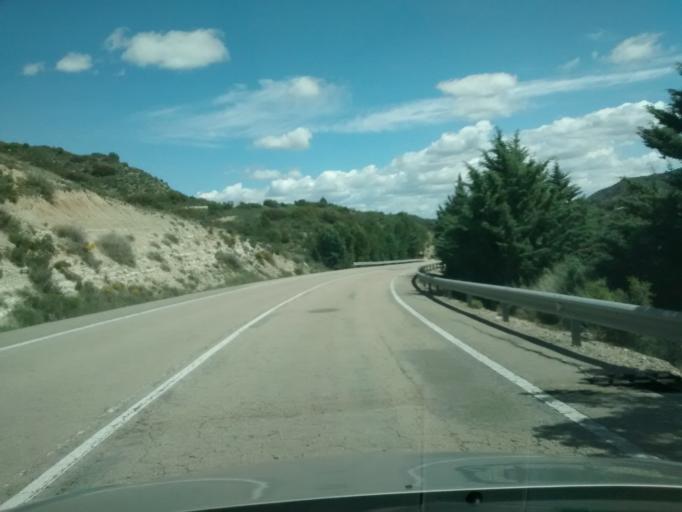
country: ES
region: Aragon
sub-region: Provincia de Huesca
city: Alcubierre
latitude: 41.8247
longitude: -0.5163
